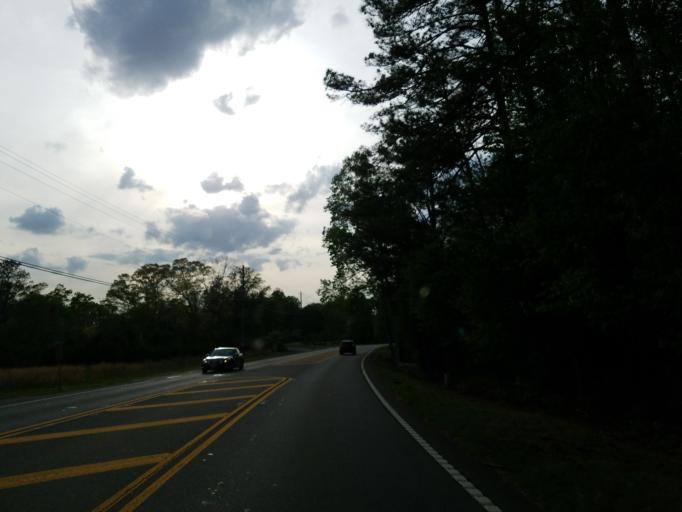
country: US
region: Georgia
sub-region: Cherokee County
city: Canton
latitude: 34.2205
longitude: -84.4656
